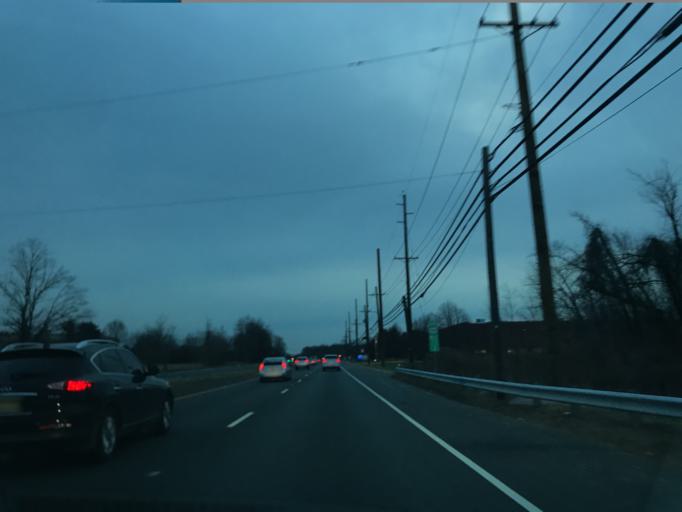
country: US
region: New Jersey
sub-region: Middlesex County
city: Cranbury
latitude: 40.3370
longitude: -74.5029
